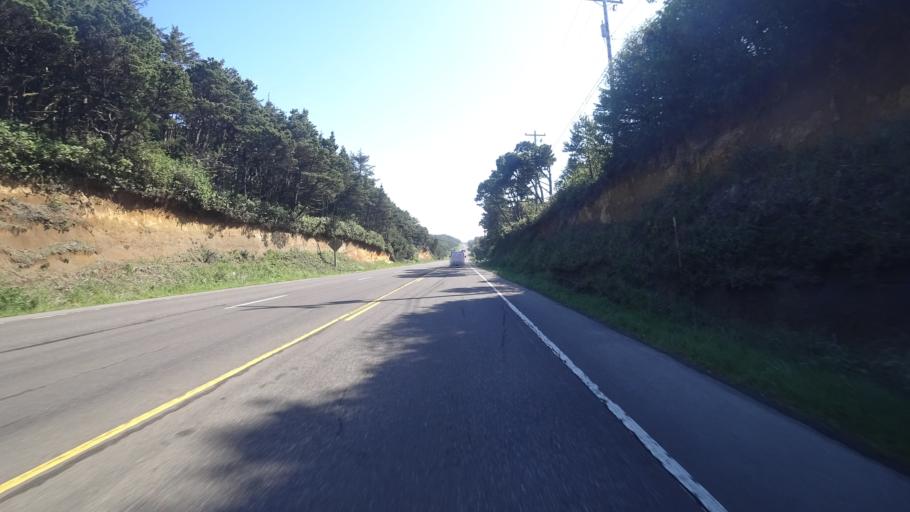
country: US
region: Oregon
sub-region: Lincoln County
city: Newport
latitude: 44.5667
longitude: -124.0688
